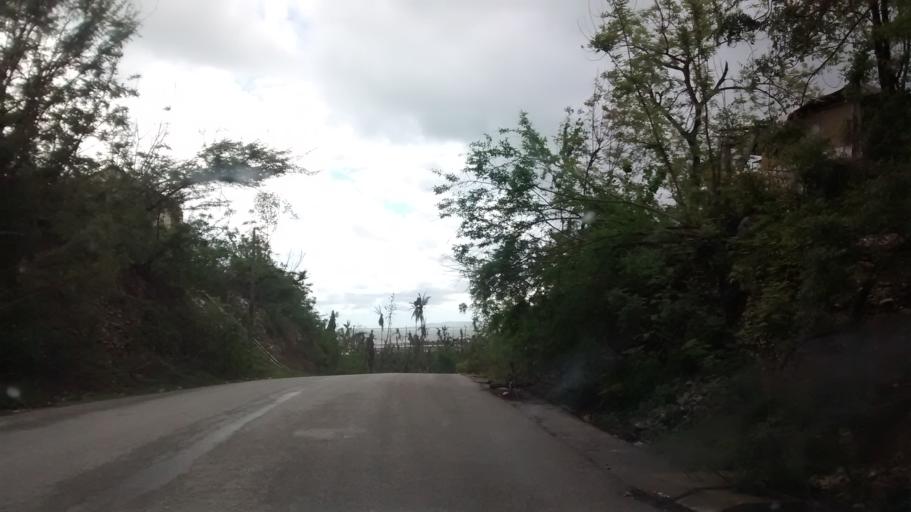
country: HT
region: Grandans
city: Jeremie
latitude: 18.6150
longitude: -74.0845
